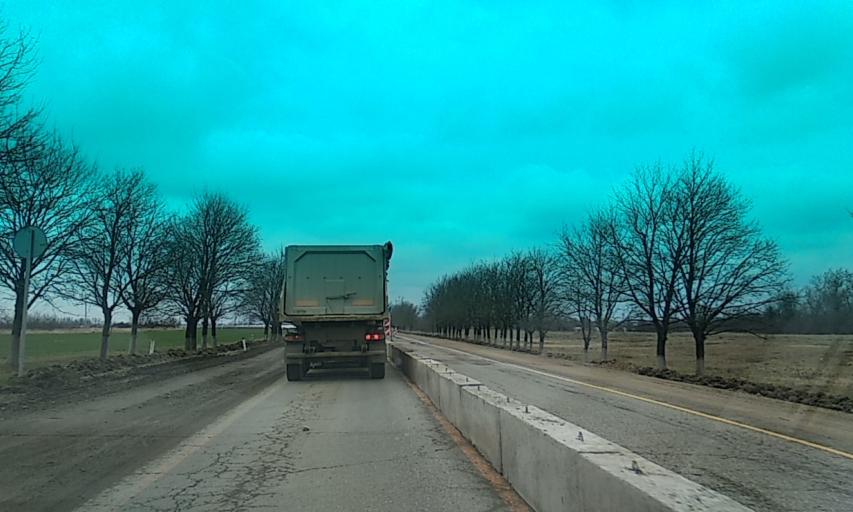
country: RU
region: Adygeya
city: Beloye
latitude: 45.0153
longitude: 39.6944
